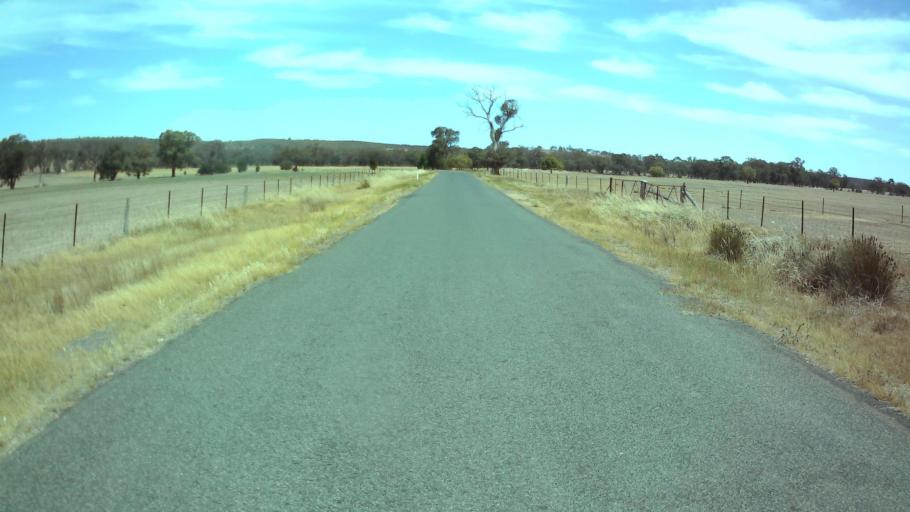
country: AU
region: New South Wales
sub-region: Weddin
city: Grenfell
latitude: -33.8408
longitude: 148.1772
